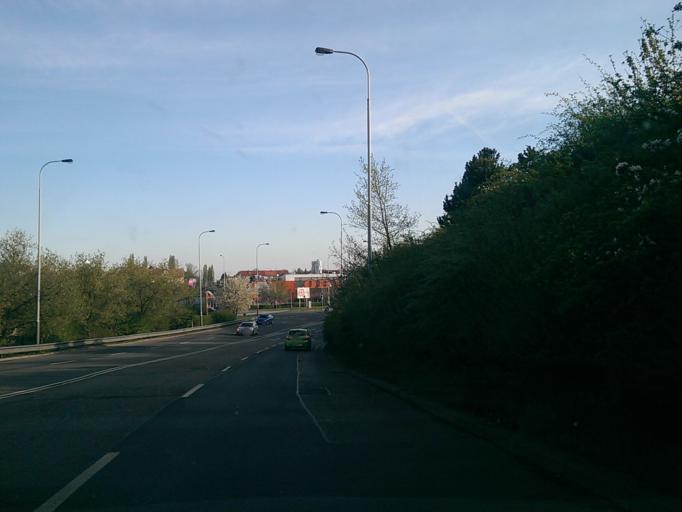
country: CZ
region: Central Bohemia
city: Vestec
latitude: 50.0371
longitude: 14.4790
